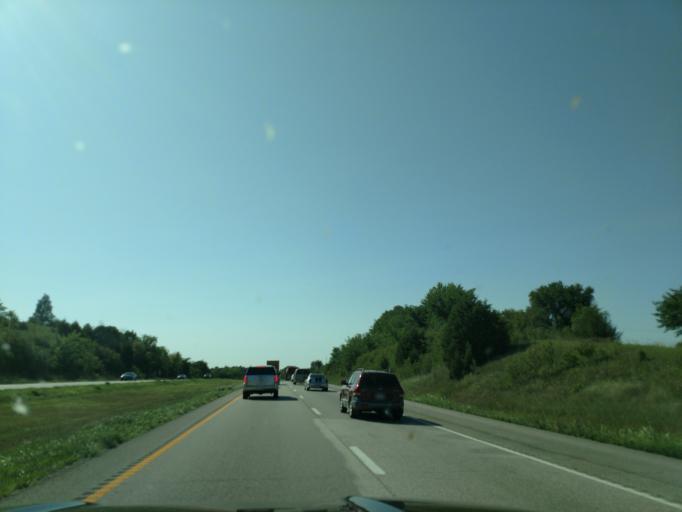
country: US
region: Missouri
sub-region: Andrew County
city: Country Club Village
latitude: 39.8777
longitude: -94.8424
